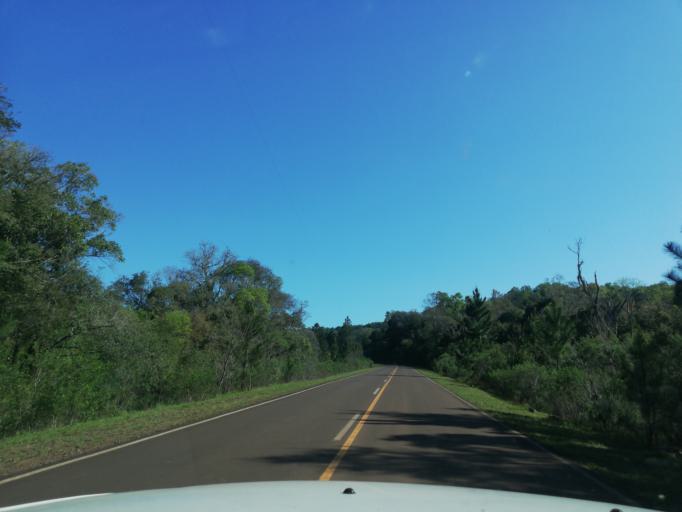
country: AR
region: Misiones
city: Arroyo del Medio
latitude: -27.6682
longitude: -55.4001
